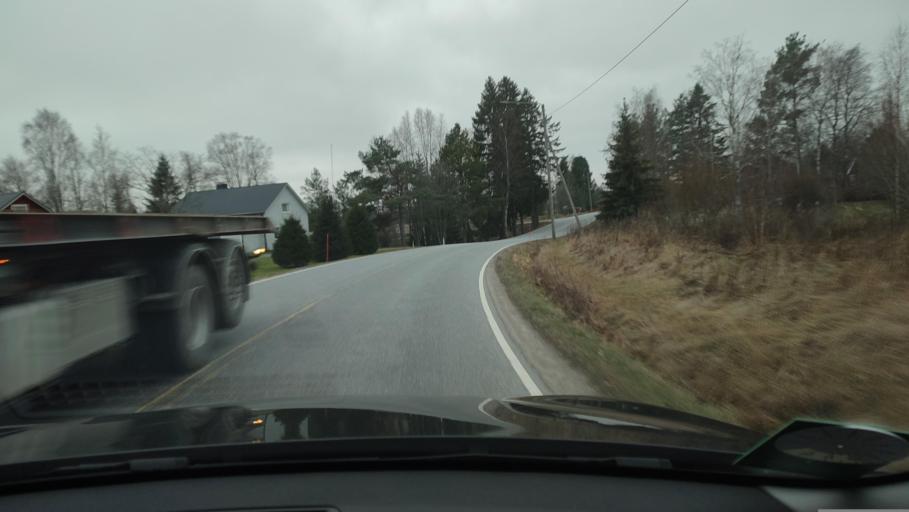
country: FI
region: Southern Ostrobothnia
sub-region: Suupohja
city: Karijoki
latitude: 62.2706
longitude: 21.7180
